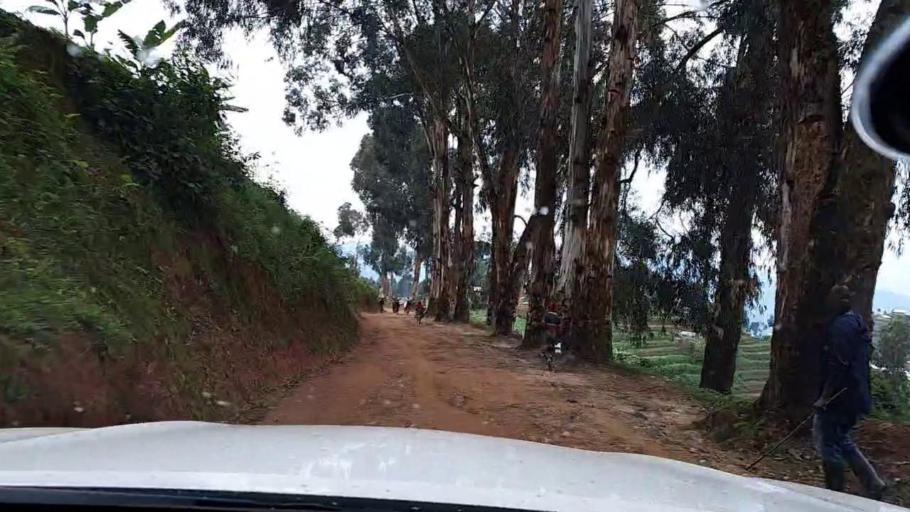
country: RW
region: Southern Province
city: Nzega
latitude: -2.3796
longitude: 29.2427
